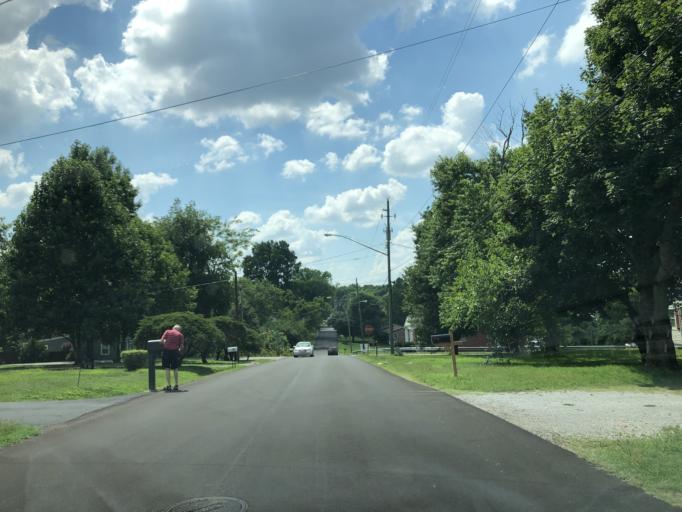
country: US
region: Tennessee
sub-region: Davidson County
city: Oak Hill
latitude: 36.1198
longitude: -86.7376
